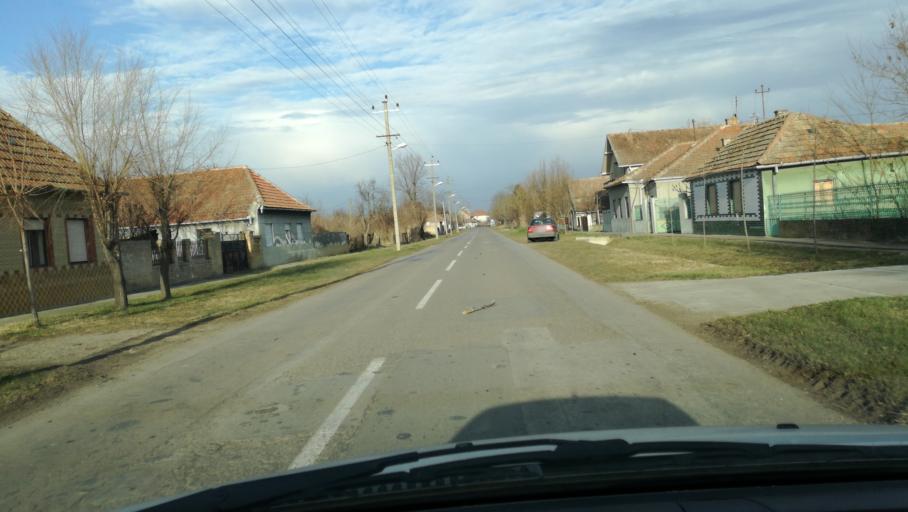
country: RS
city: Rusko Selo
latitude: 45.7655
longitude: 20.5870
